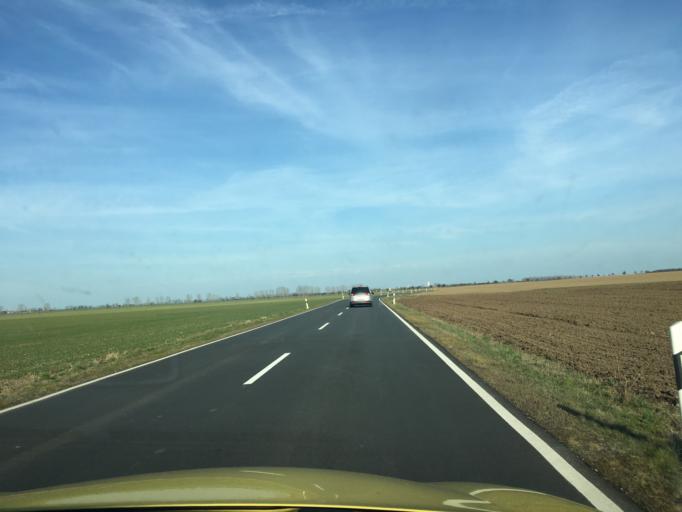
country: DE
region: Saxony-Anhalt
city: Gleina
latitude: 51.2648
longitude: 11.7683
